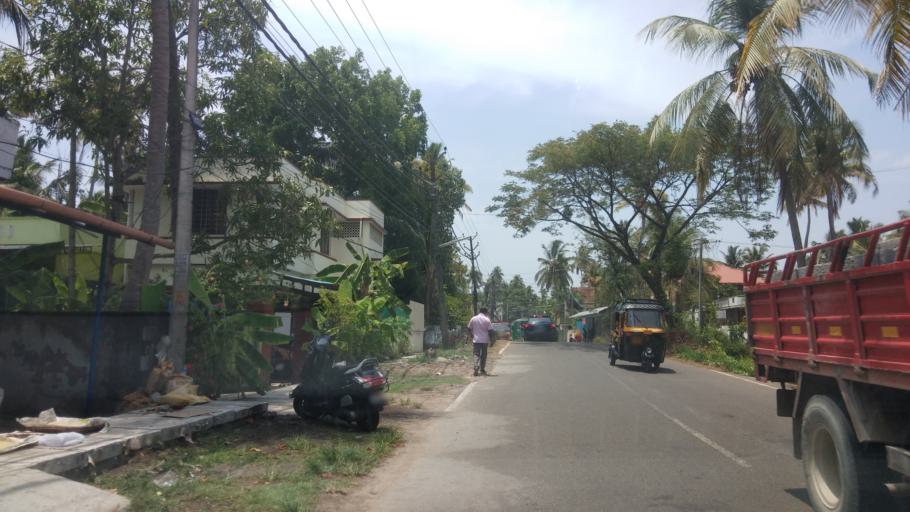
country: IN
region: Kerala
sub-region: Ernakulam
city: Cochin
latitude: 9.8922
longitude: 76.2593
